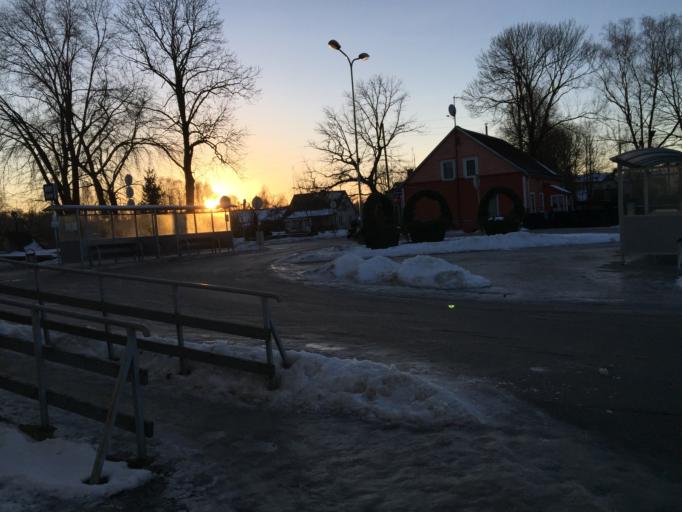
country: LV
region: Jaunjelgava
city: Jaunjelgava
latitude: 56.6177
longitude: 25.0891
